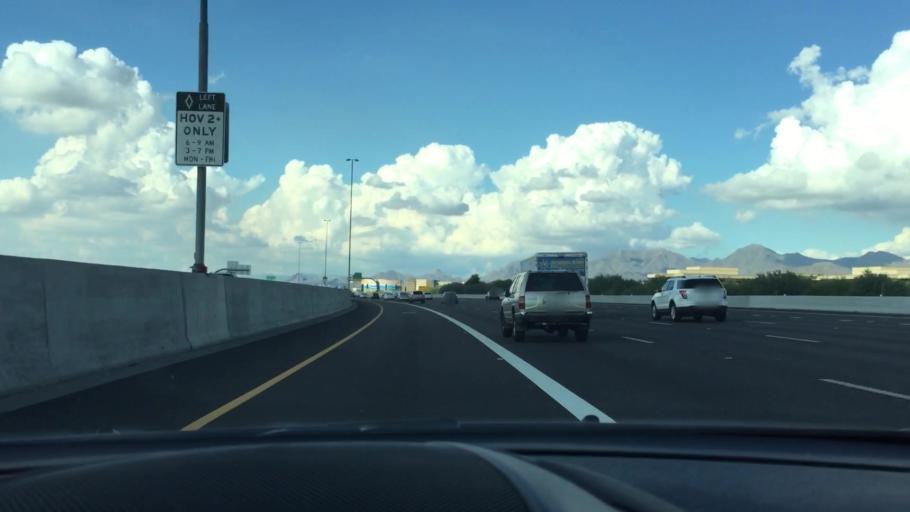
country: US
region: Arizona
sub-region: Maricopa County
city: Scottsdale
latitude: 33.5452
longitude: -111.8786
